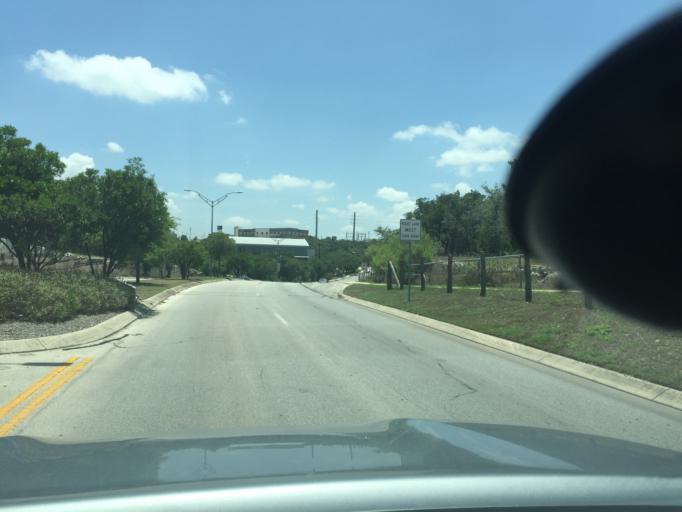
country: US
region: Texas
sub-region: Bexar County
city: Timberwood Park
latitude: 29.6847
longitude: -98.4590
